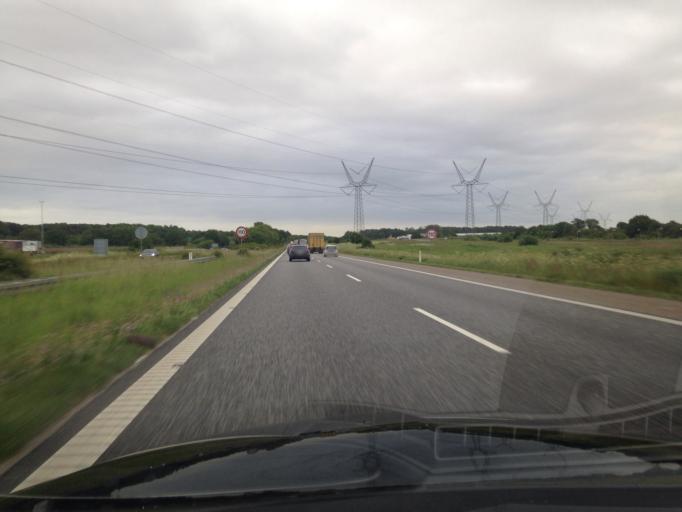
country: DK
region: South Denmark
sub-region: Fredericia Kommune
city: Taulov
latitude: 55.5389
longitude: 9.6484
